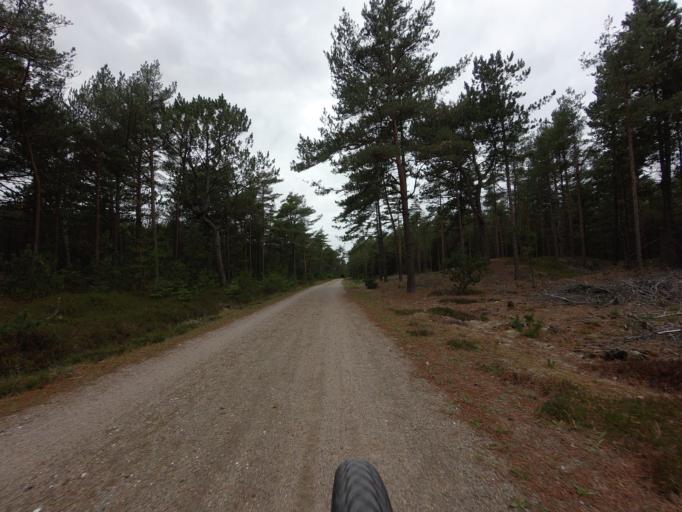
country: DK
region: North Denmark
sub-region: Hjorring Kommune
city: Sindal
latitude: 57.6075
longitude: 10.2605
